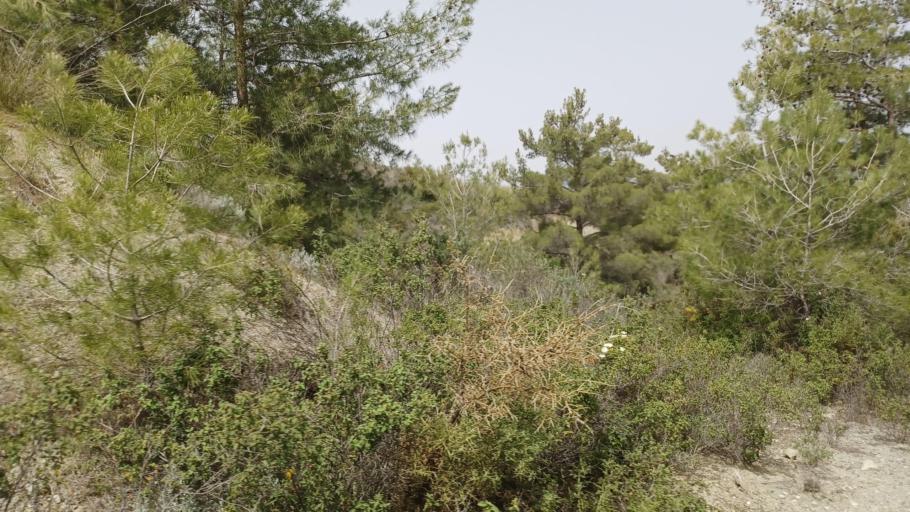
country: CY
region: Limassol
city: Parekklisha
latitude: 34.8291
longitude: 33.0951
